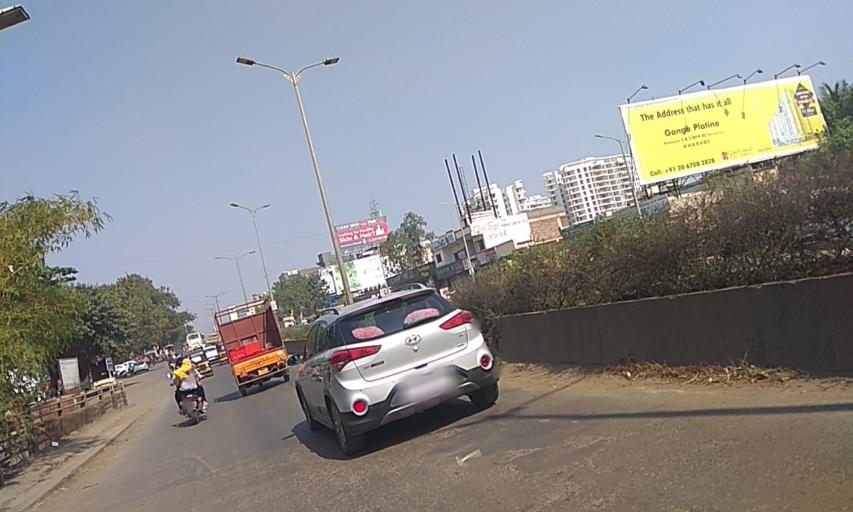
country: IN
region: Maharashtra
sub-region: Pune Division
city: Lohogaon
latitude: 18.5373
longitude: 73.9340
